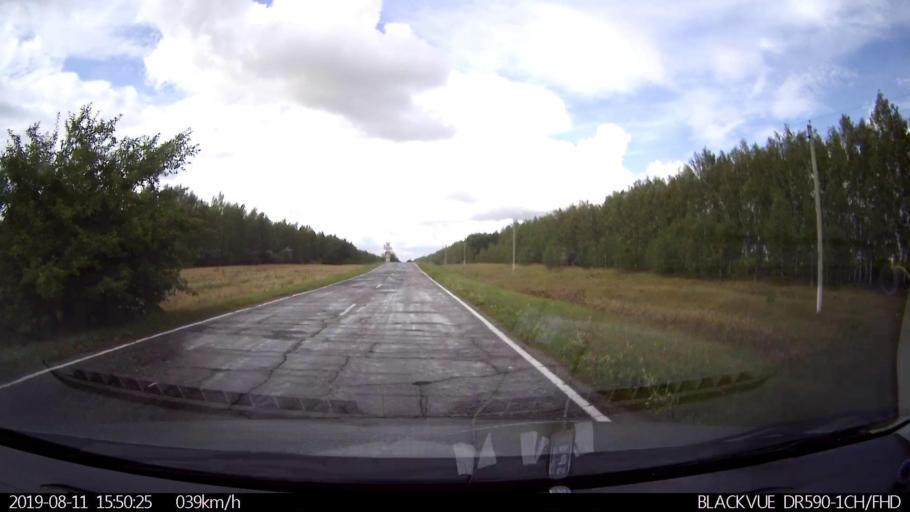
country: RU
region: Ulyanovsk
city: Ignatovka
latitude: 53.9118
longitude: 47.6558
